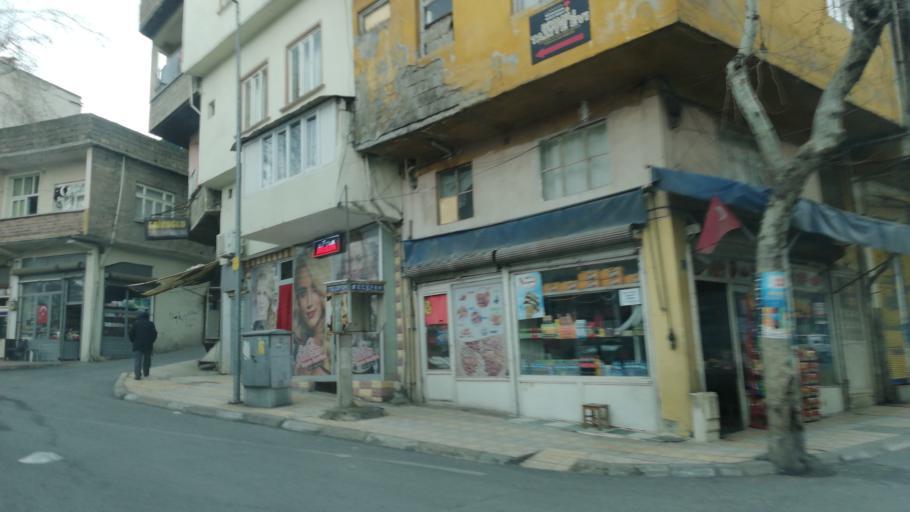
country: TR
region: Kahramanmaras
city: Kahramanmaras
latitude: 37.5834
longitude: 36.9338
